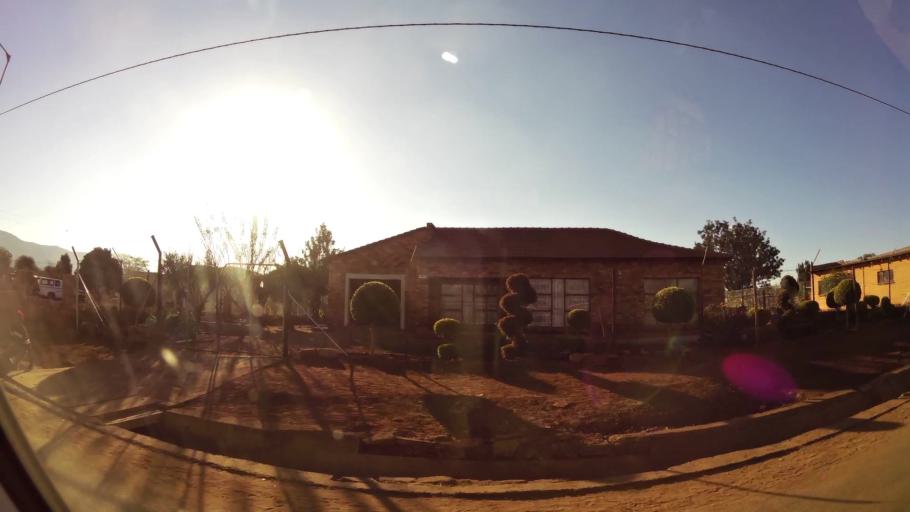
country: ZA
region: Limpopo
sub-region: Waterberg District Municipality
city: Mokopane
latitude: -24.1668
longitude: 28.9870
